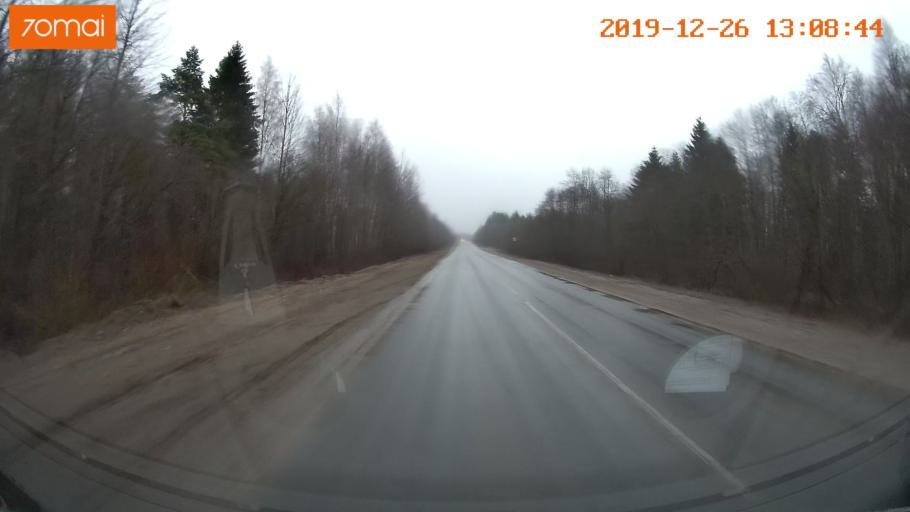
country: RU
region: Vologda
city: Cherepovets
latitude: 59.0544
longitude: 37.9416
